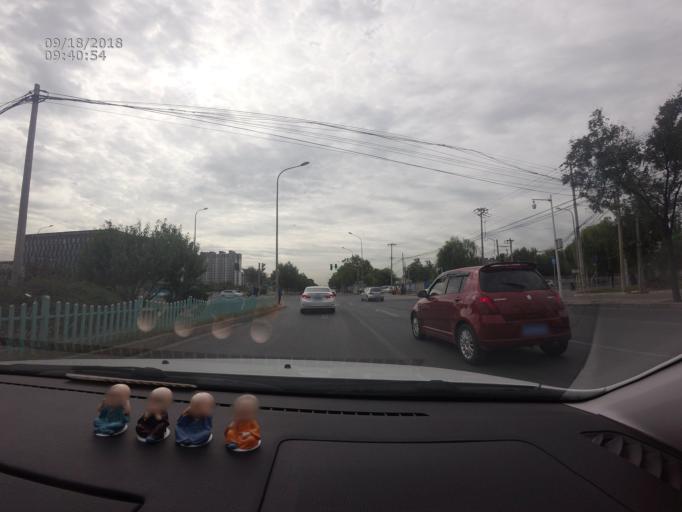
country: CN
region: Beijing
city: Xibeiwang
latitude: 40.0668
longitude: 116.2404
